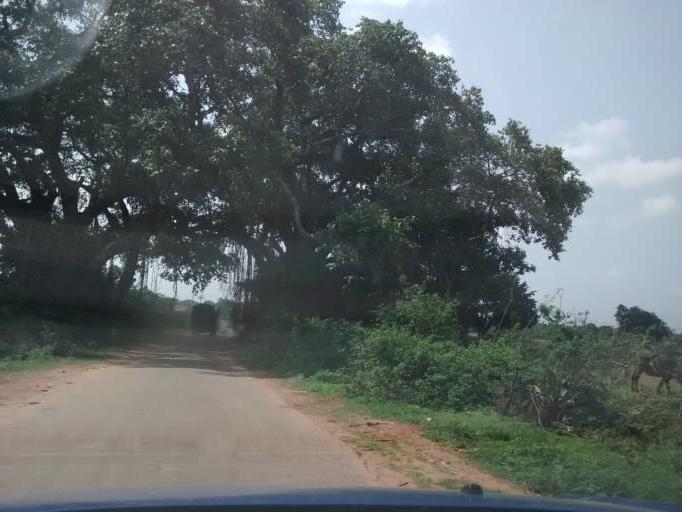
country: IN
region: Karnataka
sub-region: Hassan
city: Hole Narsipur
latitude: 12.6942
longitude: 76.1810
